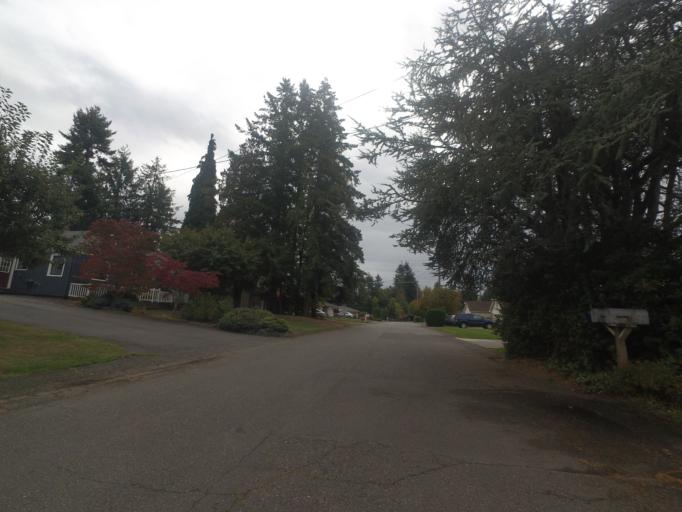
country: US
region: Washington
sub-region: Pierce County
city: University Place
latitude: 47.2146
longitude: -122.5432
